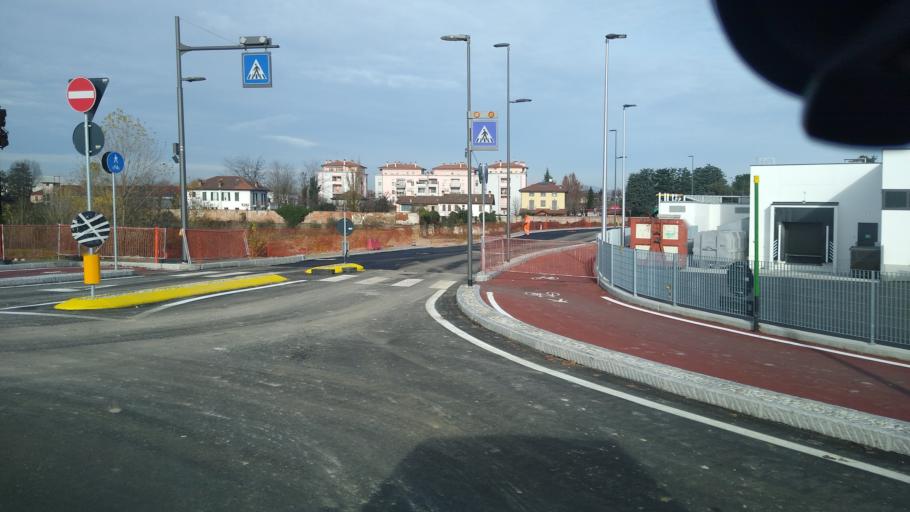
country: IT
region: Lombardy
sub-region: Provincia di Bergamo
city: Treviglio
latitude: 45.5166
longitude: 9.5849
